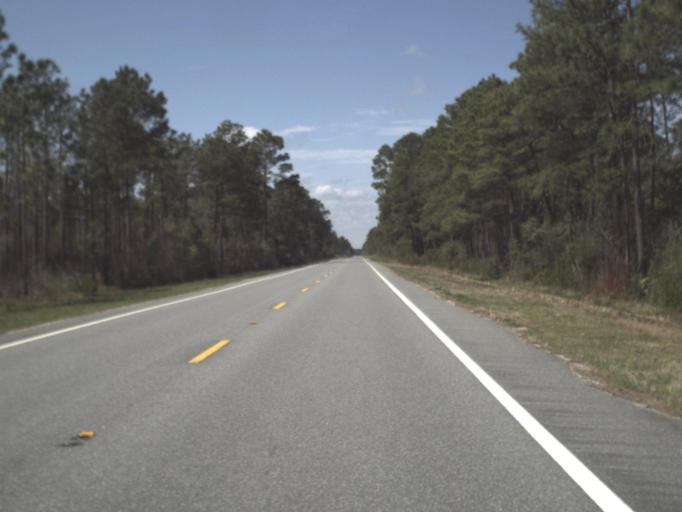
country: US
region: Florida
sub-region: Gadsden County
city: Midway
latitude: 30.3440
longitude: -84.4988
